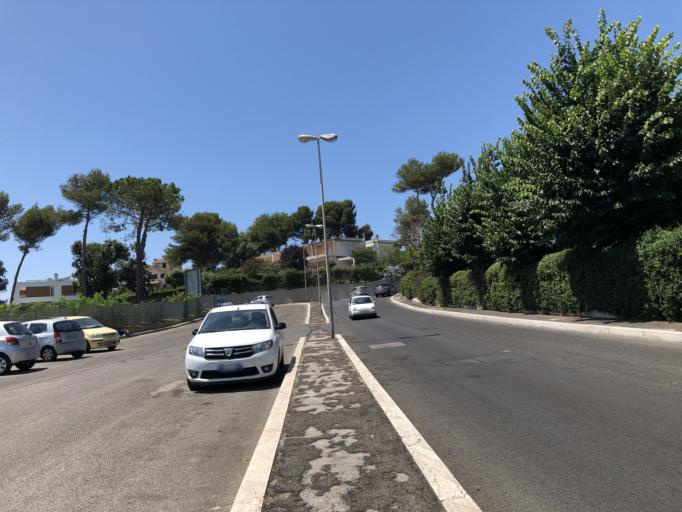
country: IT
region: Latium
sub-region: Citta metropolitana di Roma Capitale
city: Nettuno
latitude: 41.4579
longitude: 12.6502
